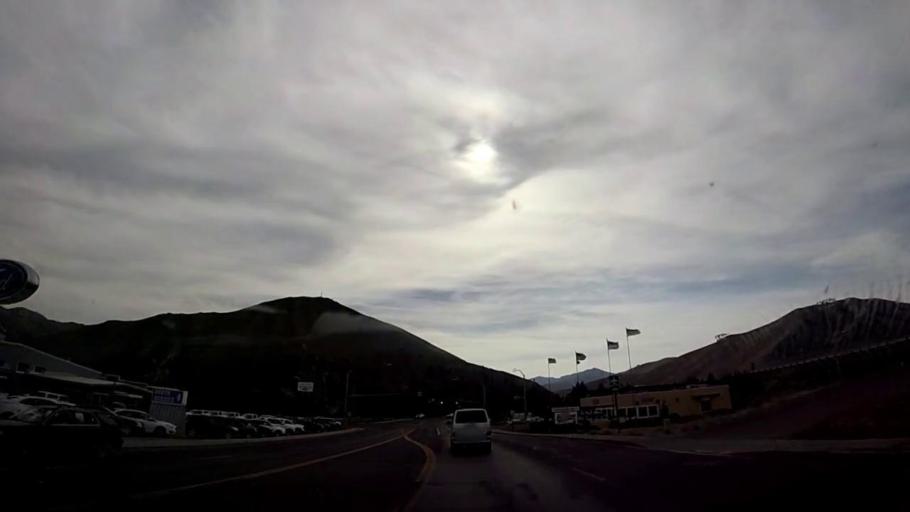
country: US
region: Idaho
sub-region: Blaine County
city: Hailey
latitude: 43.5133
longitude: -114.3063
